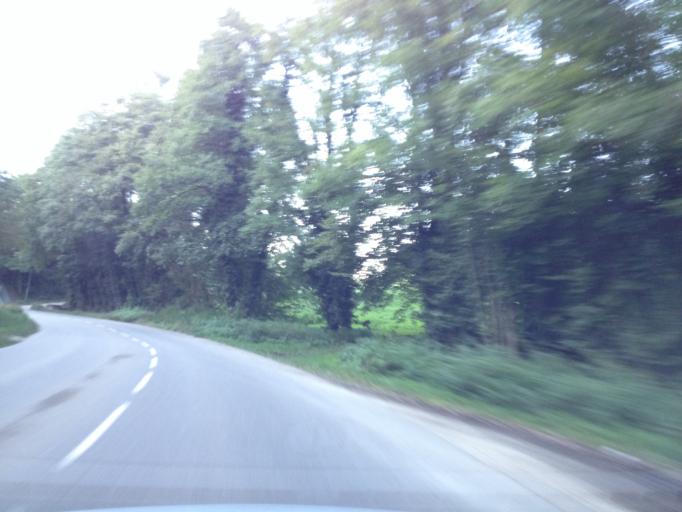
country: FR
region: Rhone-Alpes
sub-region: Departement de la Savoie
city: La Motte-Servolex
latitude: 45.6088
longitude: 5.8939
